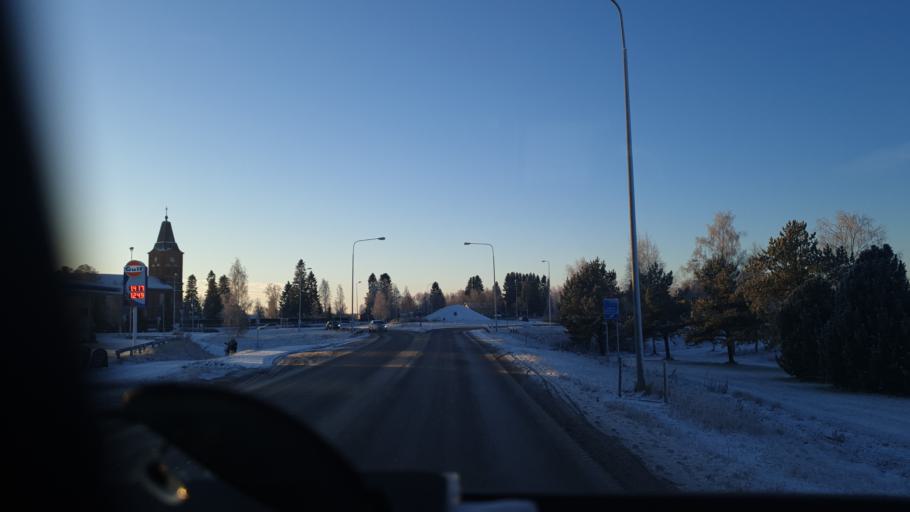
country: FI
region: Northern Ostrobothnia
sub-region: Ylivieska
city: Kalajoki
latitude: 64.2566
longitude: 23.9390
